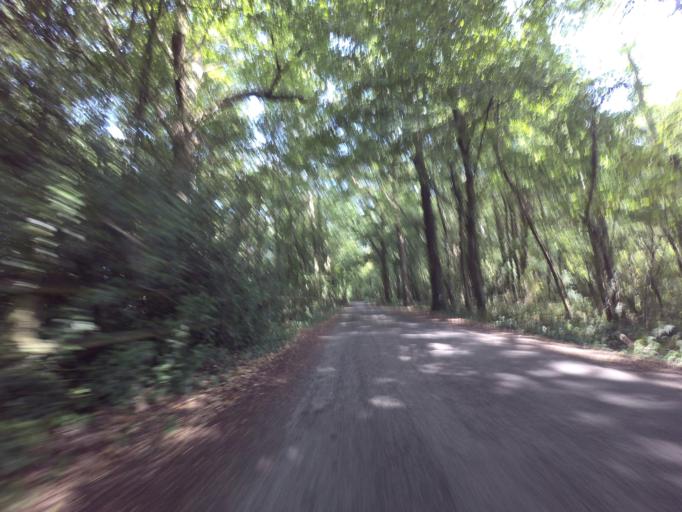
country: GB
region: England
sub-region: Kent
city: Staplehurst
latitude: 51.1238
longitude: 0.5866
